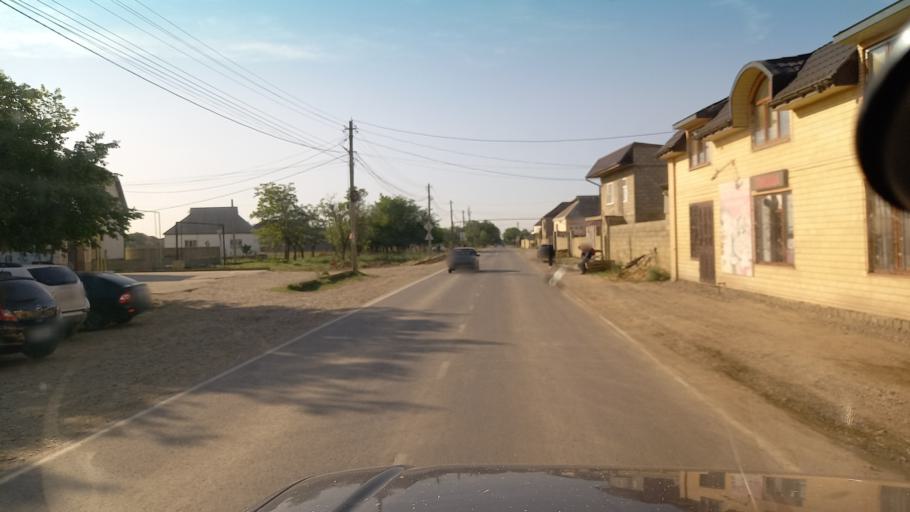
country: RU
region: Dagestan
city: Shamkhal-Termen
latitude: 43.0081
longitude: 47.3324
